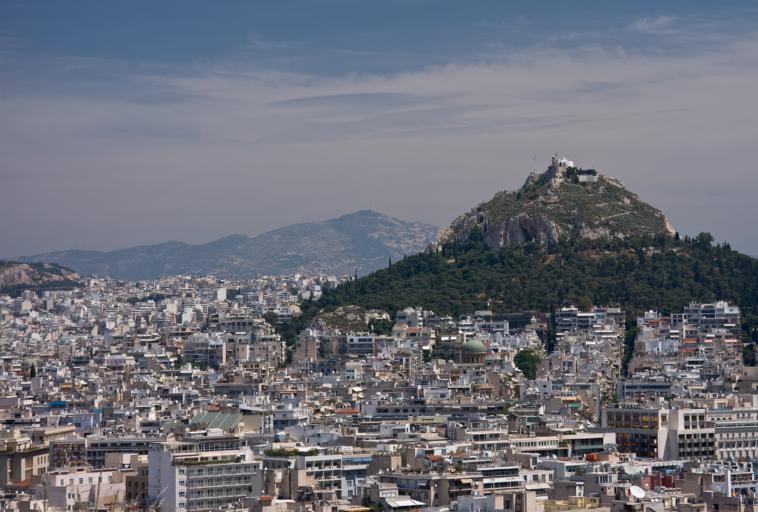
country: GR
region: Attica
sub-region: Nomarchia Athinas
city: Athens
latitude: 37.9721
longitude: 23.7275
